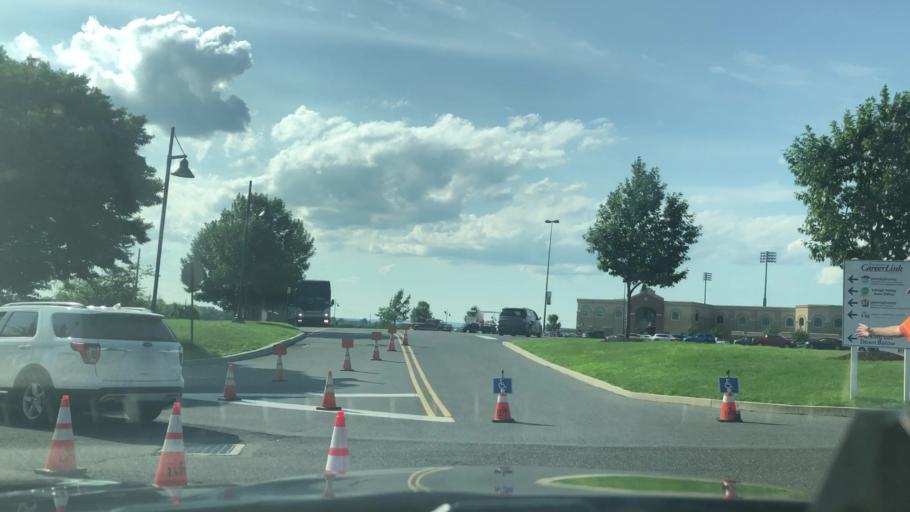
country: US
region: Pennsylvania
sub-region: Lehigh County
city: Fullerton
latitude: 40.6232
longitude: -75.4516
